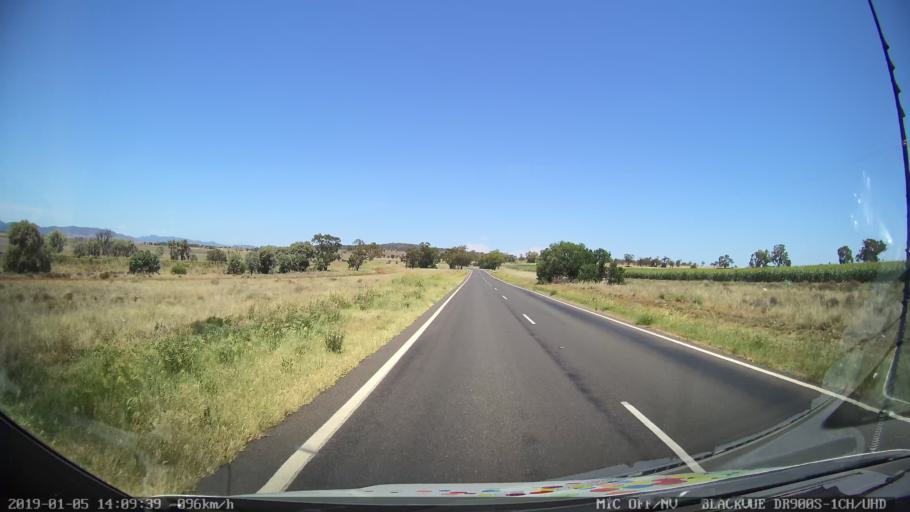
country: AU
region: New South Wales
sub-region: Gunnedah
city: Gunnedah
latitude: -31.2442
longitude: 150.4301
